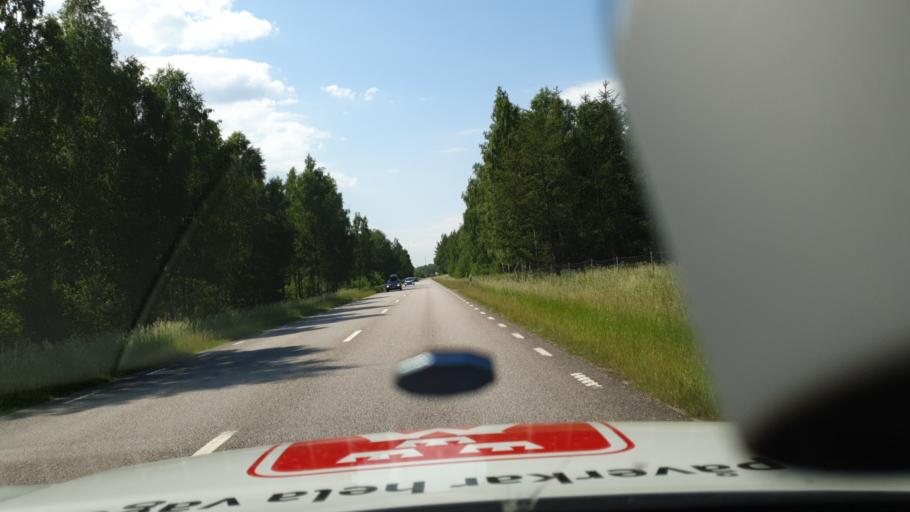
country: SE
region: Vaestra Goetaland
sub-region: Hjo Kommun
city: Hjo
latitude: 58.2474
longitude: 14.2318
